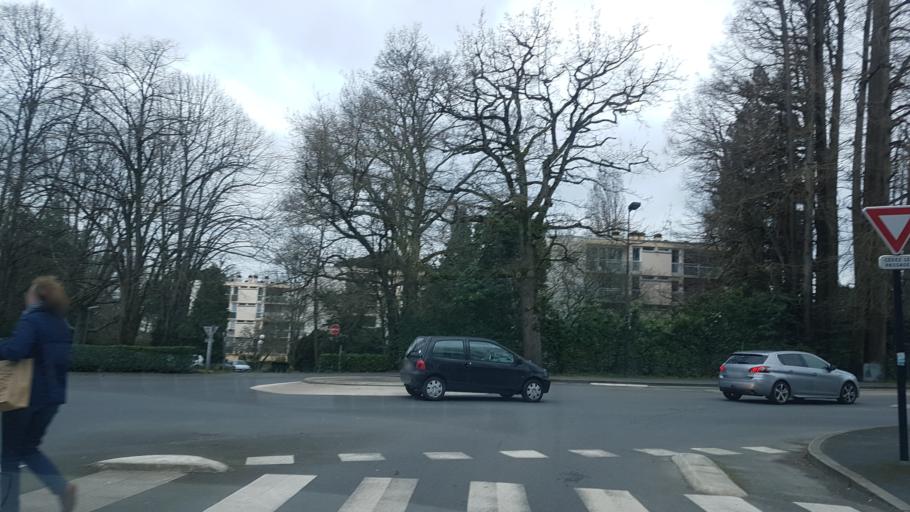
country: FR
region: Pays de la Loire
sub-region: Departement de la Loire-Atlantique
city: Nantes
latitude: 47.2498
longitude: -1.5296
